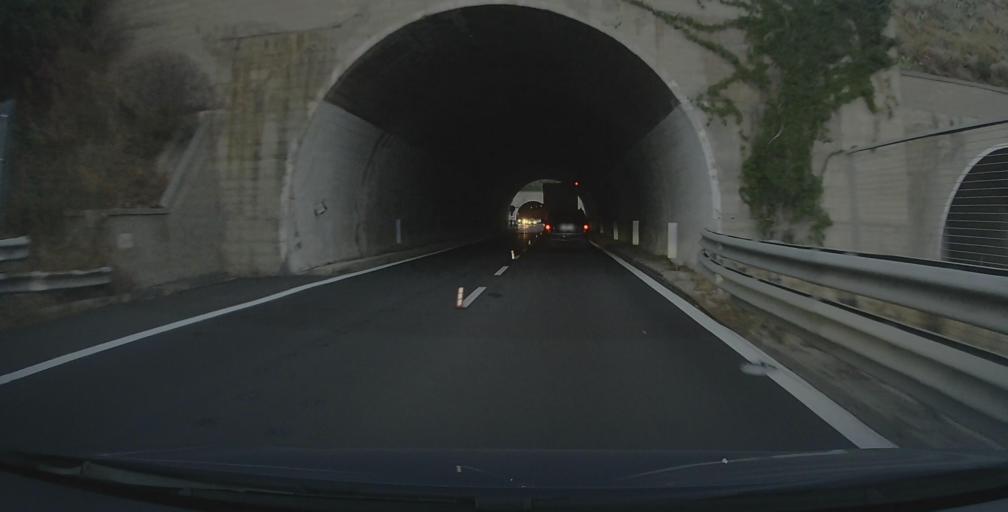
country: IT
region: Sicily
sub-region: Messina
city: Scaletta Zanclea
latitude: 38.0504
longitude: 15.4682
